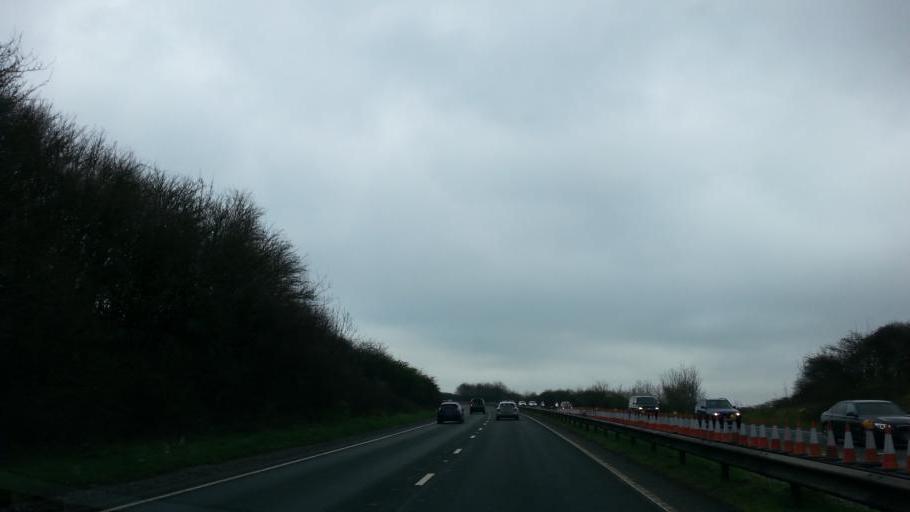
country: GB
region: England
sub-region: Devon
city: Cullompton
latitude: 50.9194
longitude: -3.4115
